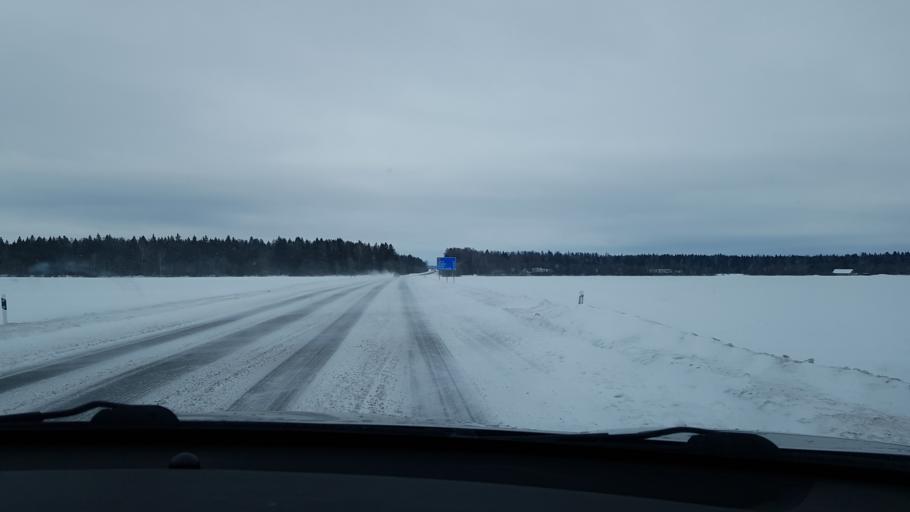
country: EE
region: Jaervamaa
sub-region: Jaerva-Jaani vald
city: Jarva-Jaani
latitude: 59.1393
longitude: 25.7701
